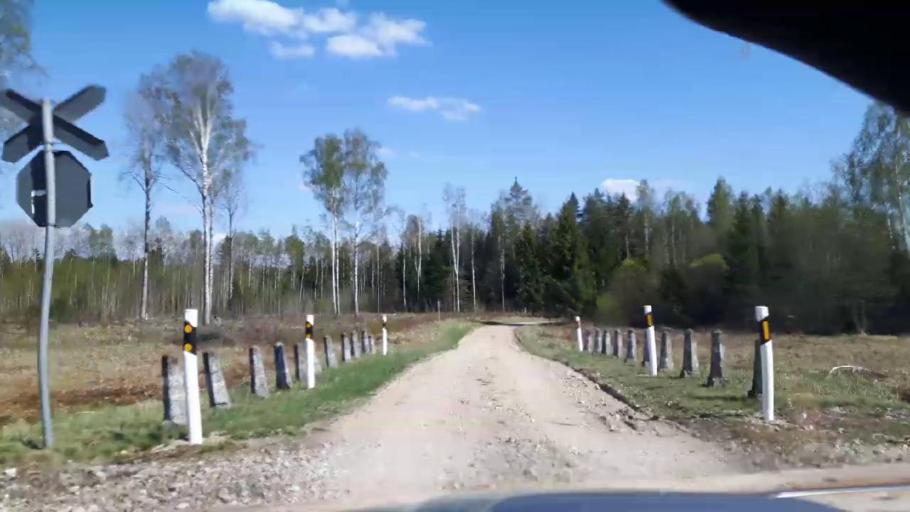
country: EE
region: Paernumaa
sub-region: Tootsi vald
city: Tootsi
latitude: 58.5404
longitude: 24.8131
